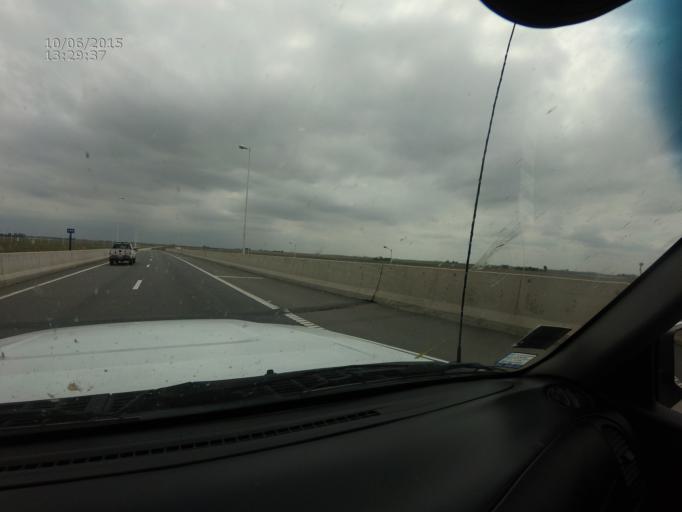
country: AR
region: Cordoba
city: Leones
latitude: -32.6374
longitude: -62.2478
